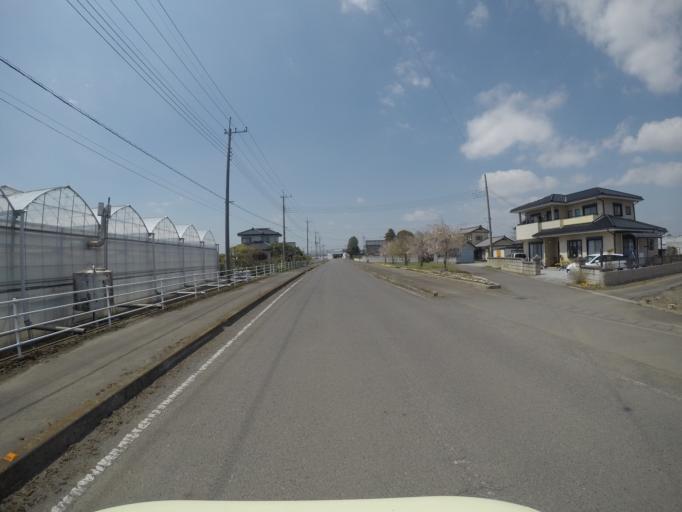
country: JP
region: Tochigi
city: Mibu
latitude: 36.4396
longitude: 139.7796
